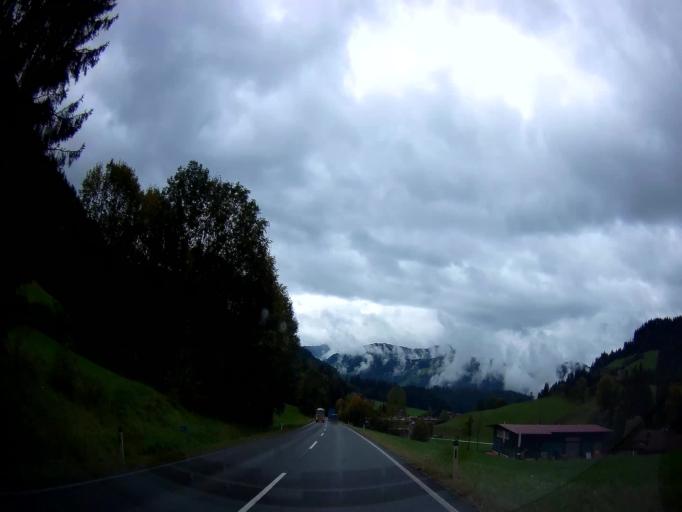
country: AT
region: Tyrol
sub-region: Politischer Bezirk Kufstein
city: Soll
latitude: 47.4910
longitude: 12.1669
